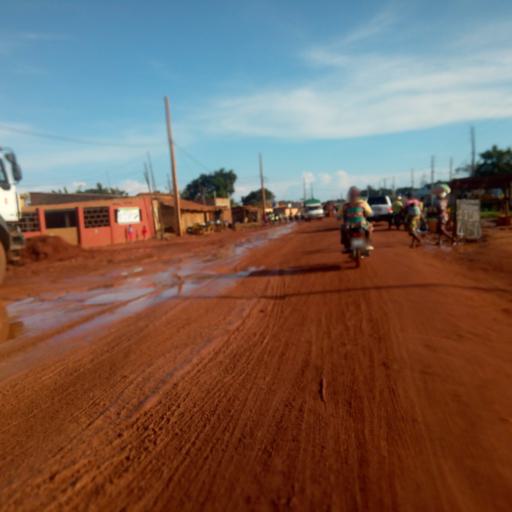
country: BJ
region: Atlantique
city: Hevie
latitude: 6.4051
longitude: 2.2669
